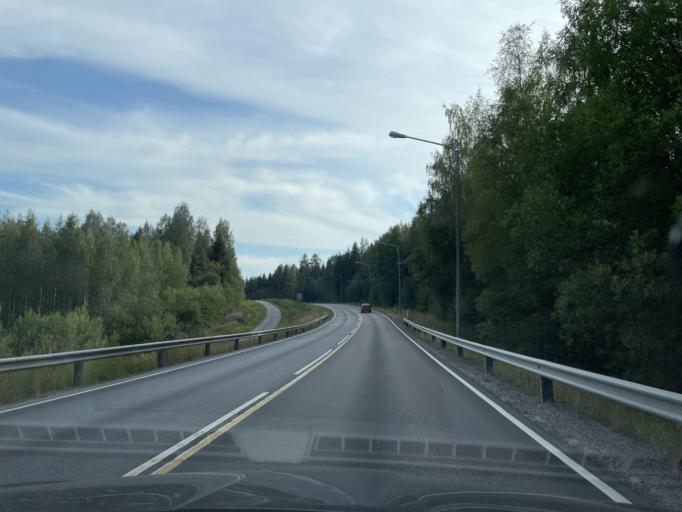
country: FI
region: Central Finland
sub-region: Jaemsae
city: Kuhmoinen
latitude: 61.5565
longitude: 25.1579
